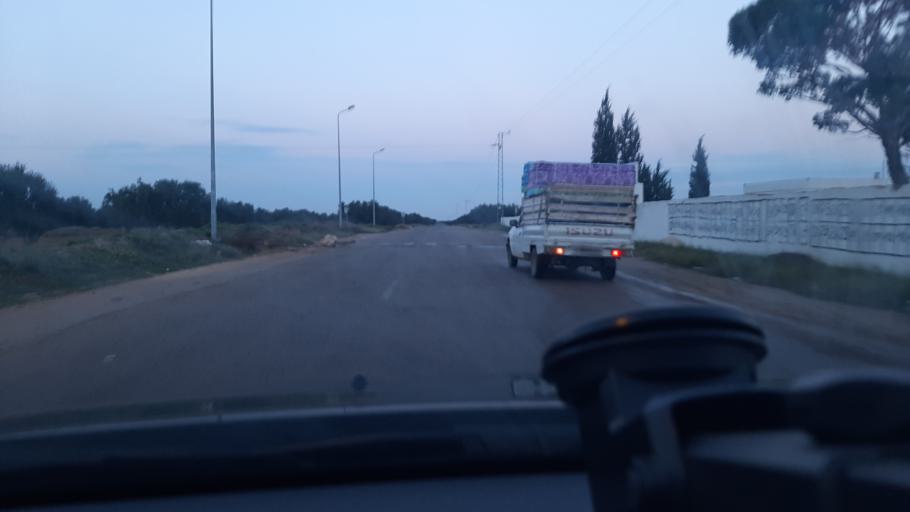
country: TN
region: Al Mahdiyah
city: Shurban
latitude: 35.0232
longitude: 10.4705
